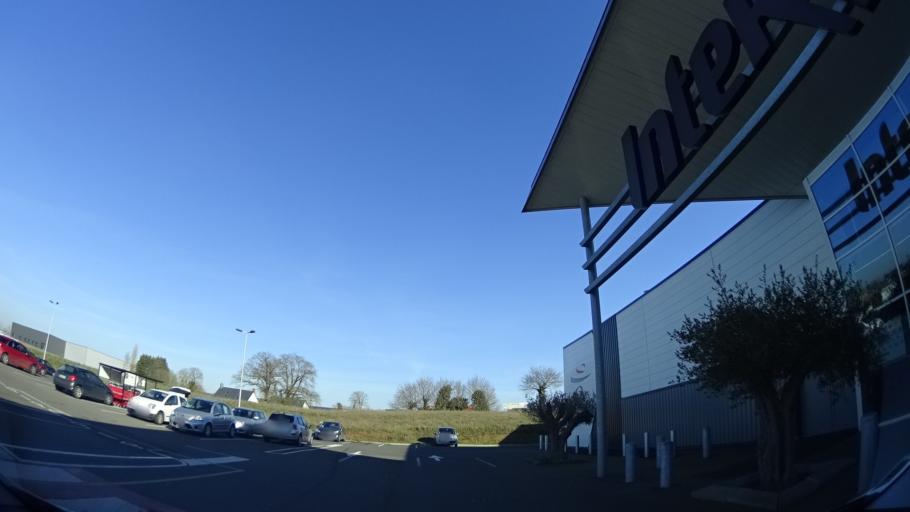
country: FR
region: Brittany
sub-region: Departement d'Ille-et-Vilaine
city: La Meziere
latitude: 48.2145
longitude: -1.7433
